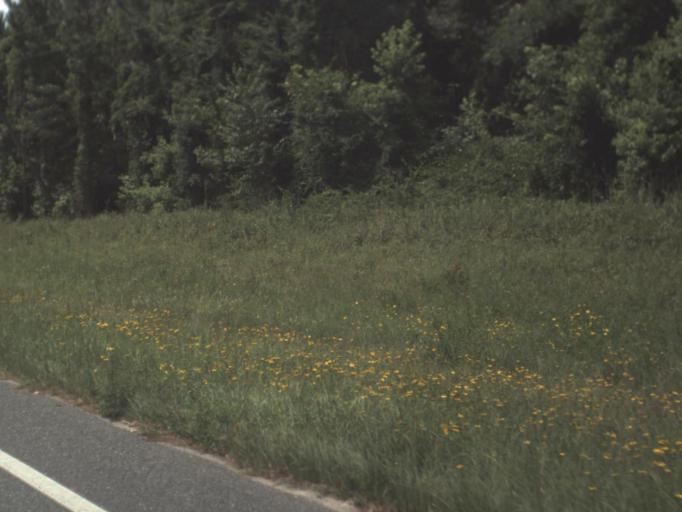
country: US
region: Florida
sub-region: Hamilton County
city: Jasper
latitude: 30.5335
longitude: -83.0453
